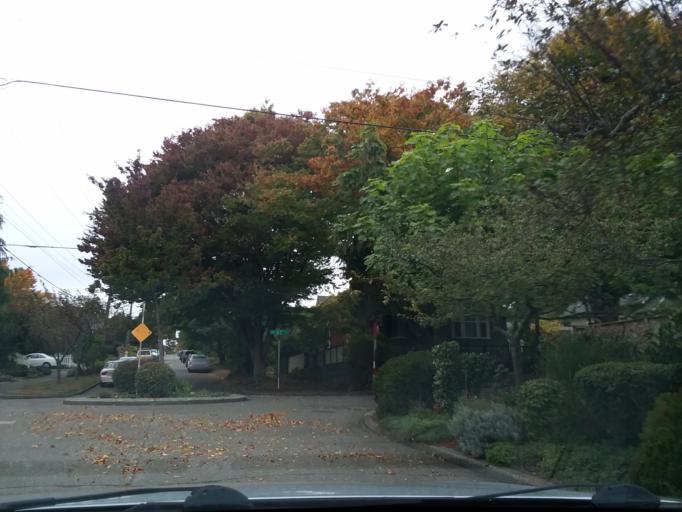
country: US
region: Washington
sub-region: King County
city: Seattle
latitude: 47.6776
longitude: -122.3789
